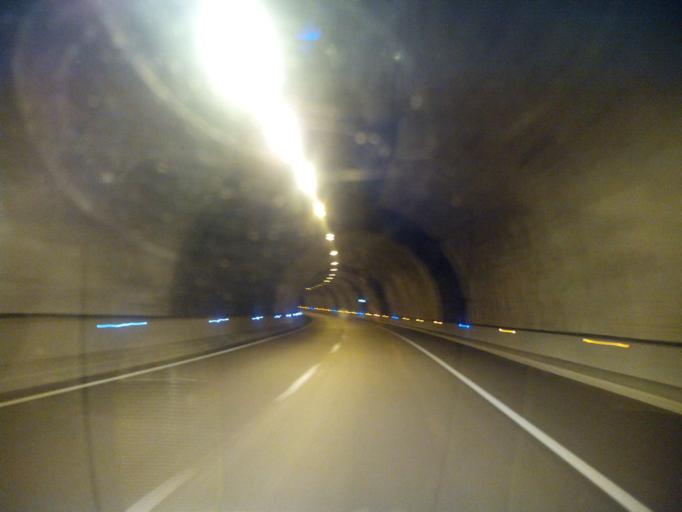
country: ES
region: Catalonia
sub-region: Provincia de Girona
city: Ripoll
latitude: 42.1723
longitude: 2.1917
